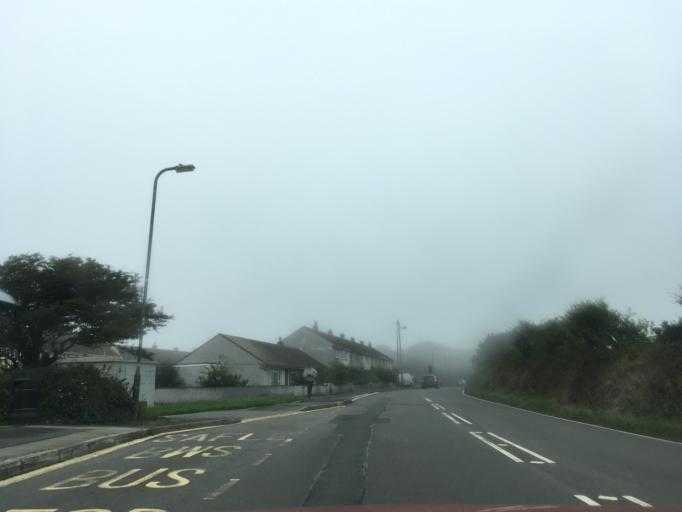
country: GB
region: Wales
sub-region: Pembrokeshire
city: Saint David's
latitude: 51.8745
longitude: -5.2020
